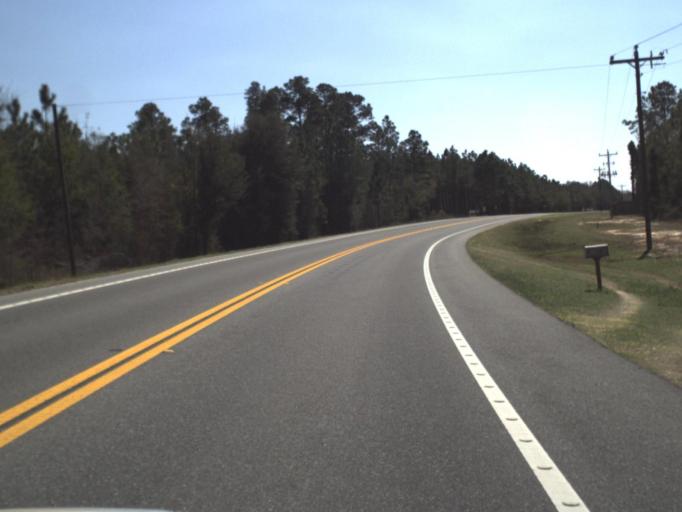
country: US
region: Florida
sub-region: Jackson County
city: Sneads
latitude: 30.6450
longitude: -85.0372
